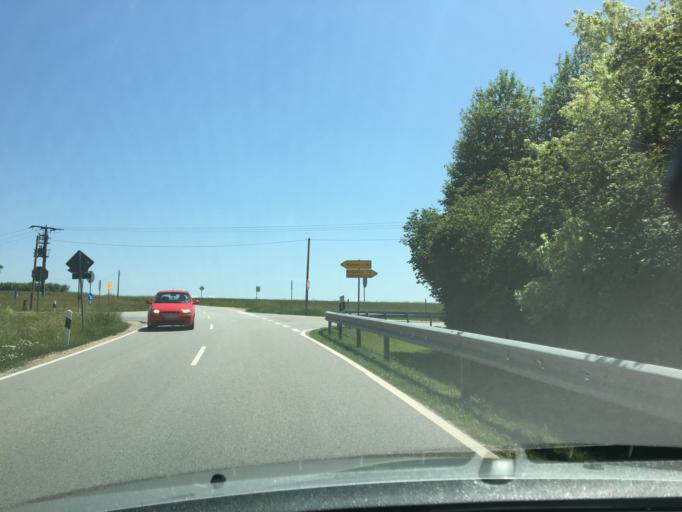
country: DE
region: Bavaria
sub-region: Upper Bavaria
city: Halsbach
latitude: 48.1330
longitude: 12.6519
